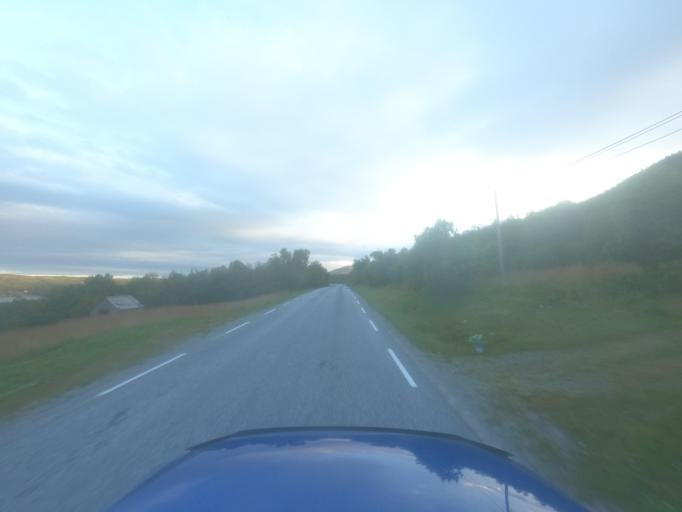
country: NO
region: Finnmark Fylke
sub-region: Porsanger
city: Lakselv
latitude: 70.3341
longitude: 25.0711
